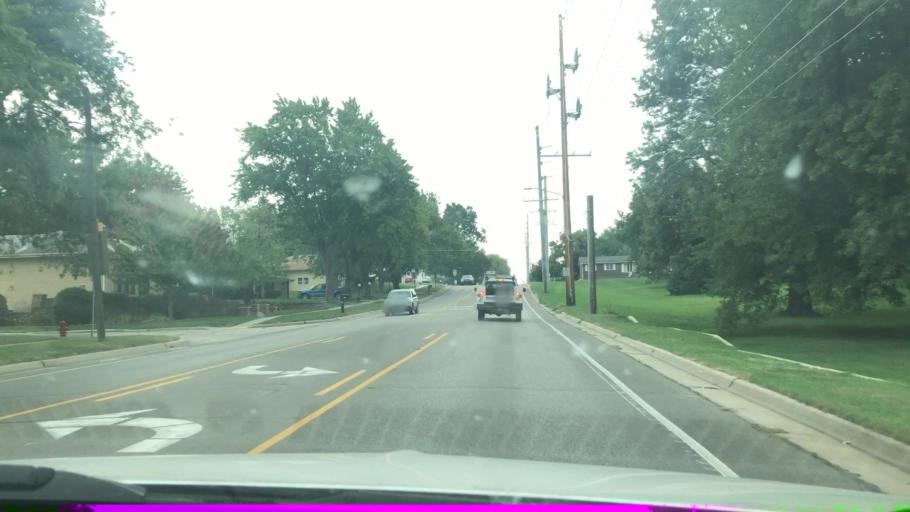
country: US
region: Iowa
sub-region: Marshall County
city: Marshalltown
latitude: 42.0225
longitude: -92.9221
